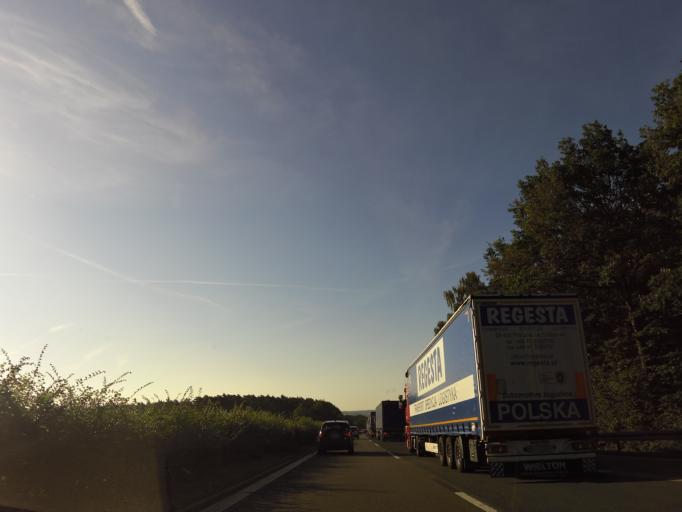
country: DE
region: Bavaria
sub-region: Regierungsbezirk Mittelfranken
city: Gremsdorf
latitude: 49.7144
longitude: 10.8414
